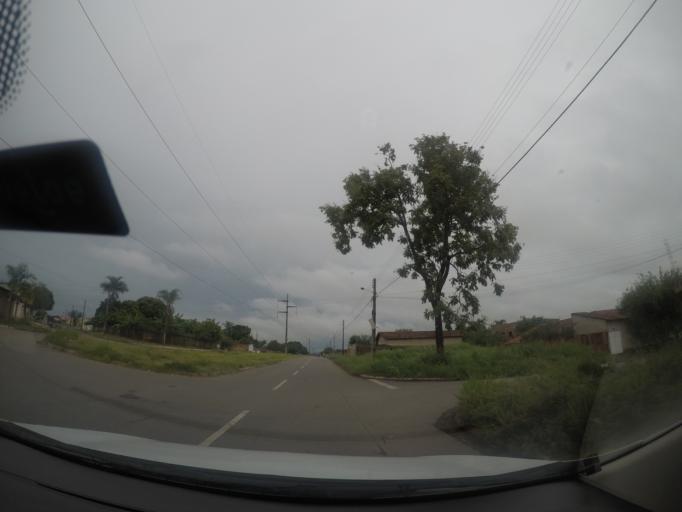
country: BR
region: Goias
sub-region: Aparecida De Goiania
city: Aparecida de Goiania
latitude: -16.7601
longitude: -49.3108
